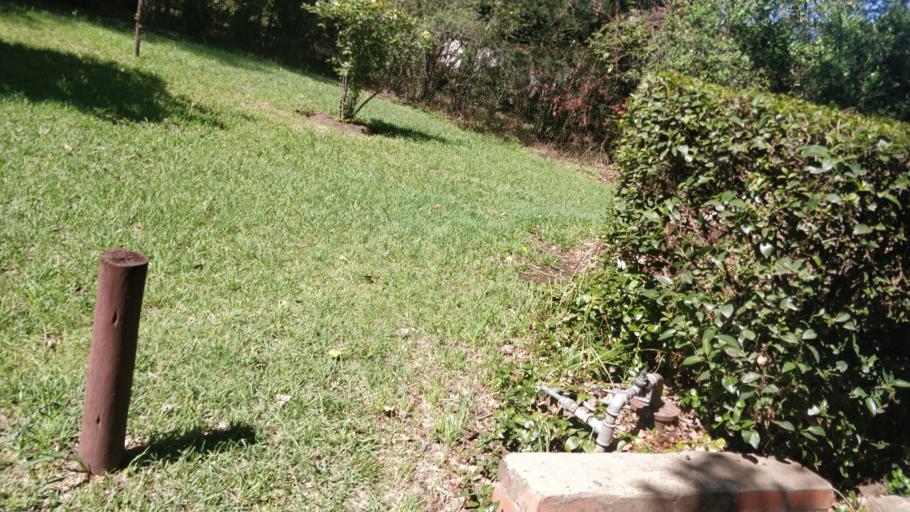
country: LS
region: Maseru
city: Nako
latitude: -29.6258
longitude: 27.5064
